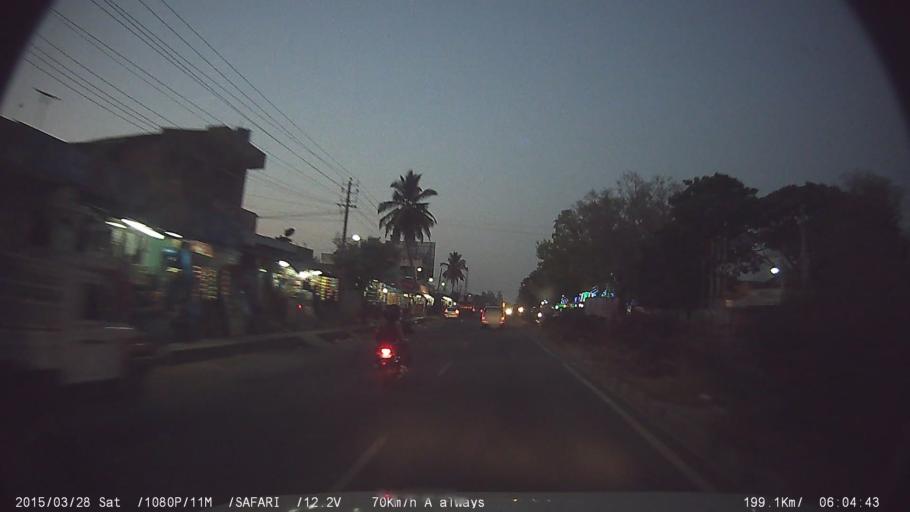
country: IN
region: Karnataka
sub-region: Ramanagara
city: Ramanagaram
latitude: 12.8303
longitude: 77.4125
